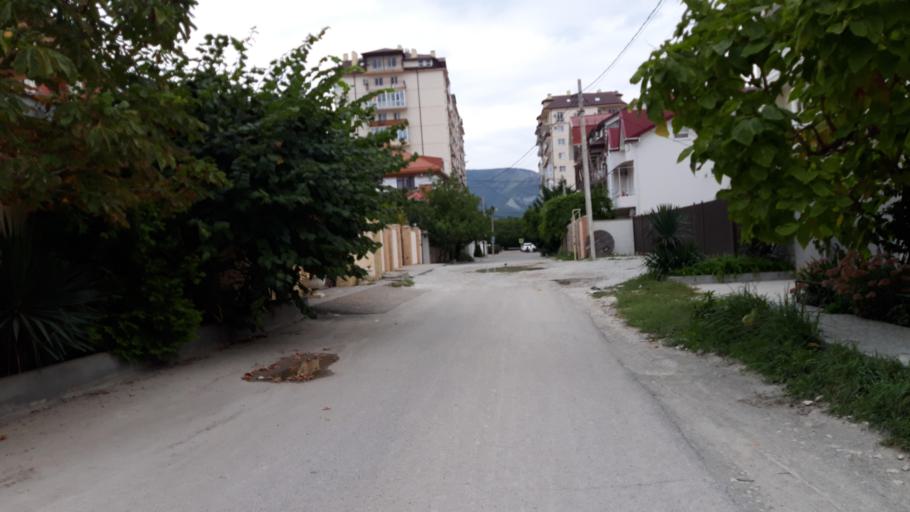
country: RU
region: Krasnodarskiy
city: Gelendzhik
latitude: 44.5510
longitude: 38.0564
